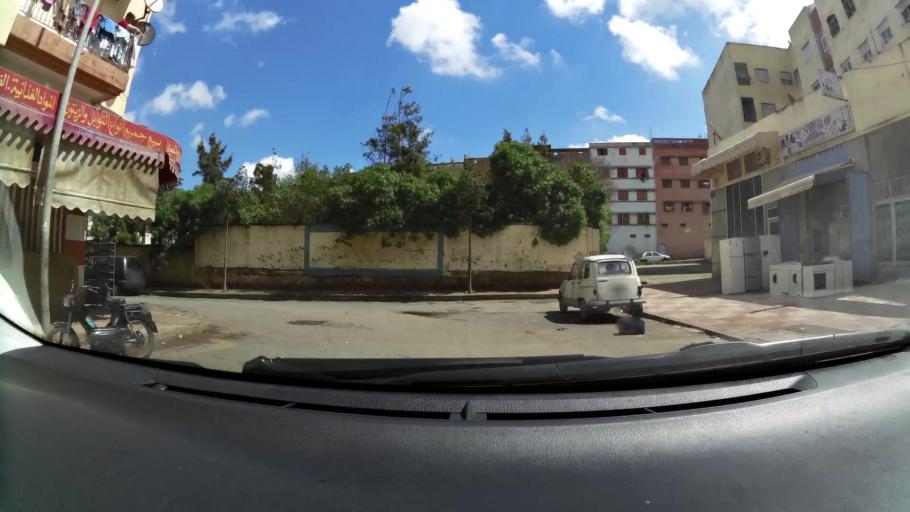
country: MA
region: Grand Casablanca
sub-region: Casablanca
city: Casablanca
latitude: 33.5375
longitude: -7.5688
